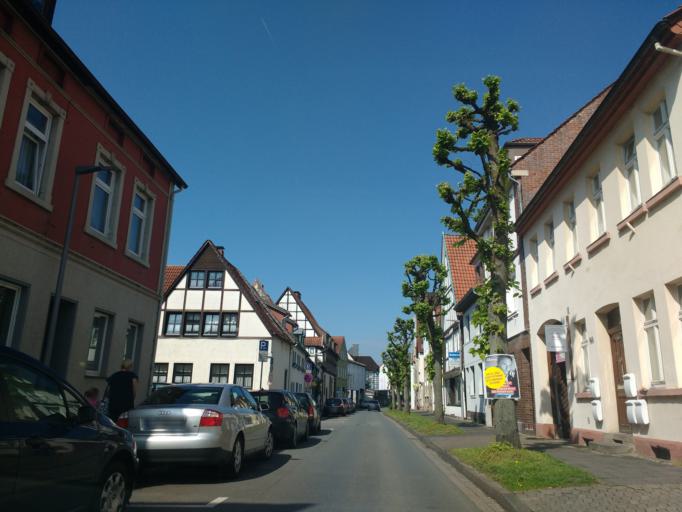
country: DE
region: North Rhine-Westphalia
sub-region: Regierungsbezirk Detmold
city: Lemgo
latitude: 52.0293
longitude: 8.8987
